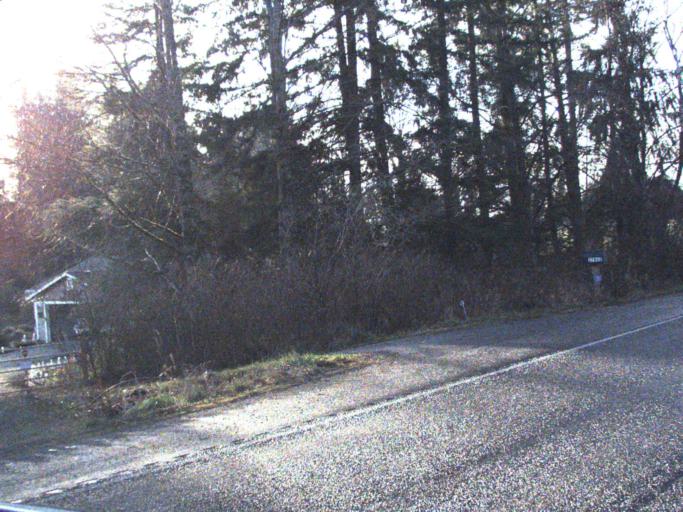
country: US
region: Washington
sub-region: Skagit County
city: Sedro-Woolley
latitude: 48.5305
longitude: -122.1434
